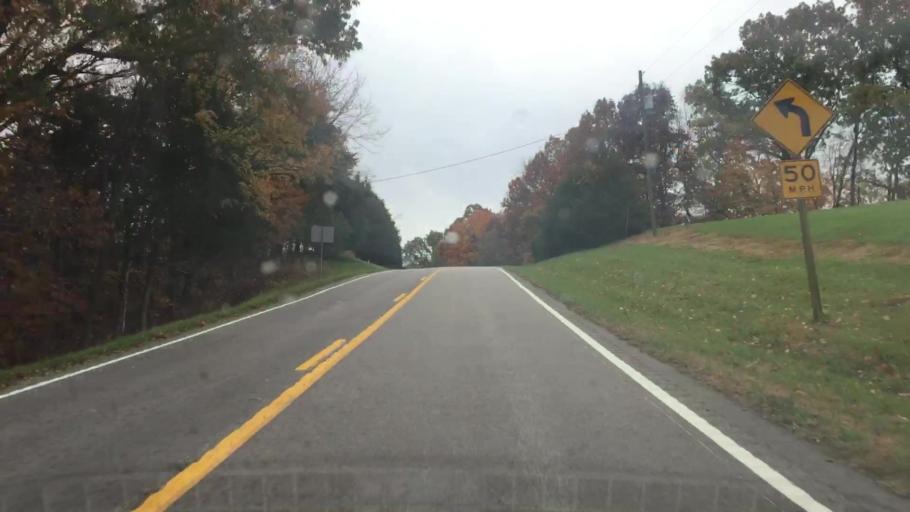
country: US
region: Missouri
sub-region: Gasconade County
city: Hermann
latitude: 38.7107
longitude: -91.6343
